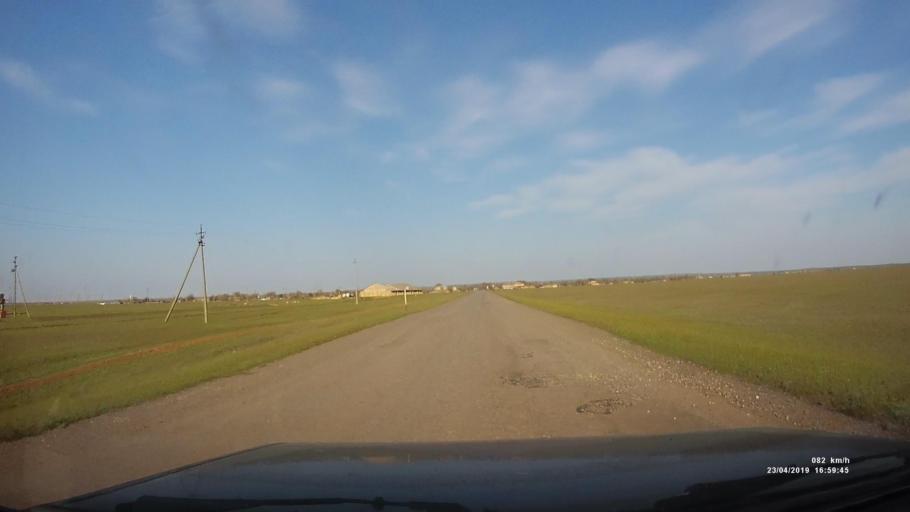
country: RU
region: Kalmykiya
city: Priyutnoye
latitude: 46.3082
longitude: 43.3958
